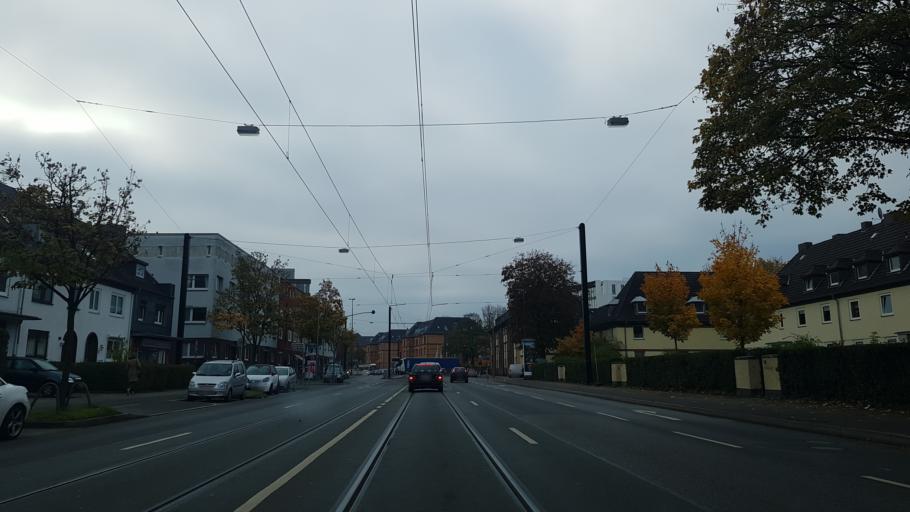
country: DE
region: North Rhine-Westphalia
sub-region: Regierungsbezirk Dusseldorf
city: Dusseldorf
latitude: 51.2555
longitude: 6.7800
